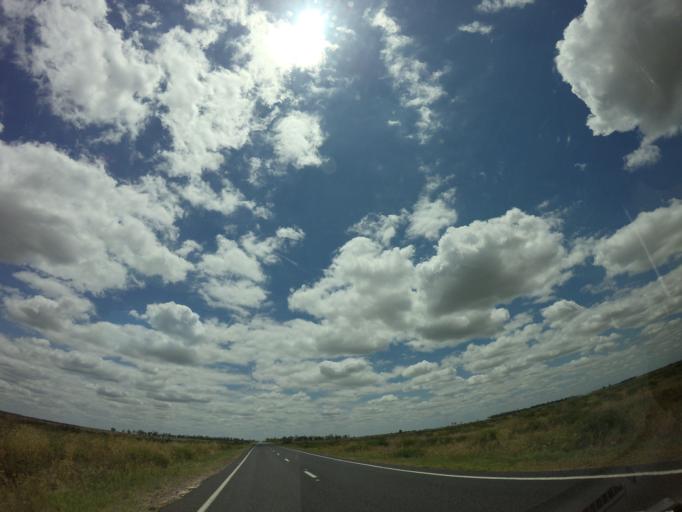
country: AU
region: New South Wales
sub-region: Moree Plains
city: Boggabilla
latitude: -28.6907
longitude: 150.2939
